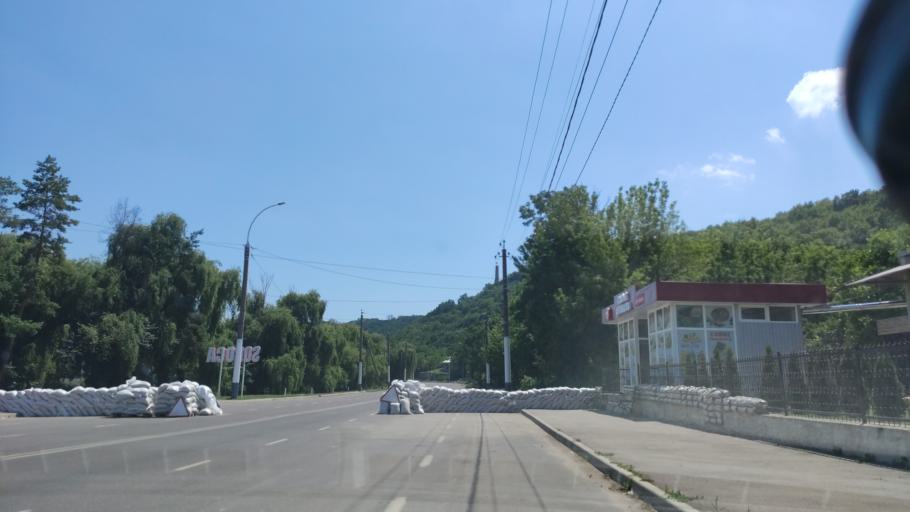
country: MD
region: Raionul Soroca
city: Soroca
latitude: 48.1432
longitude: 28.3025
